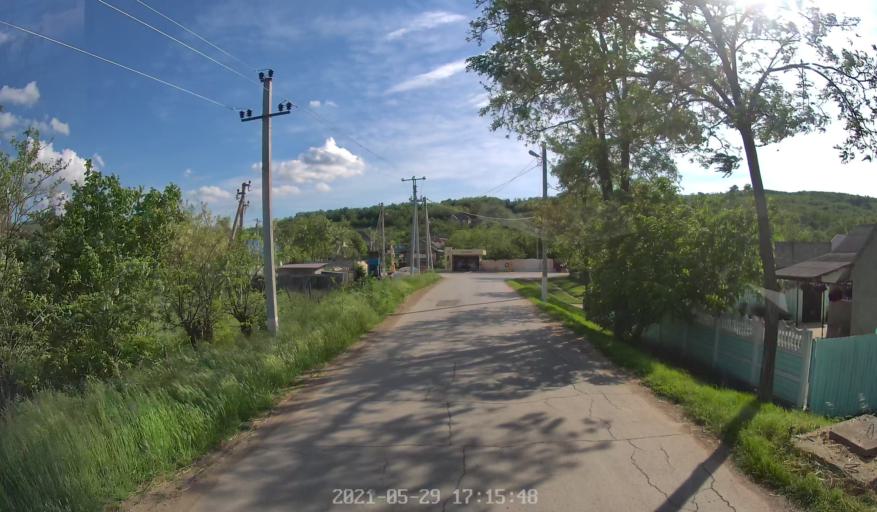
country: MD
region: Laloveni
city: Ialoveni
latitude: 46.8298
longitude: 28.8433
